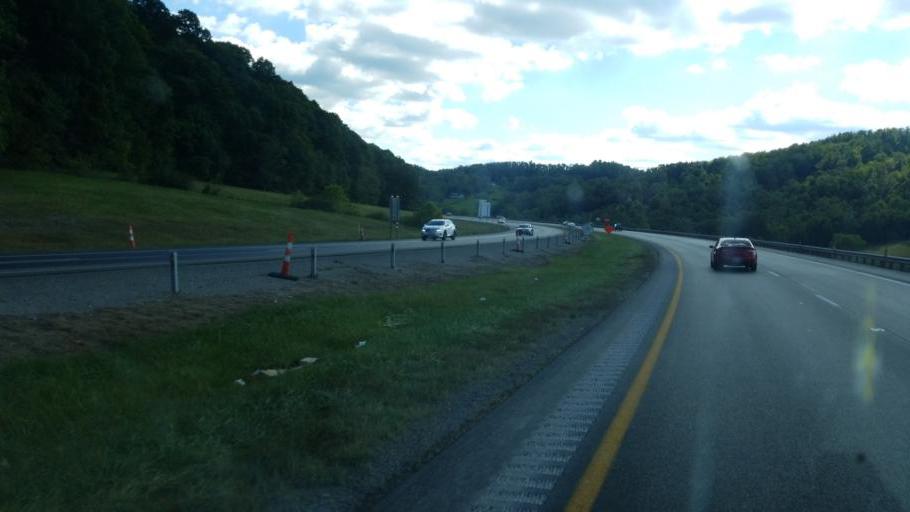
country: US
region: West Virginia
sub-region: Monongalia County
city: Brookhaven
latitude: 39.6073
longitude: -79.9307
